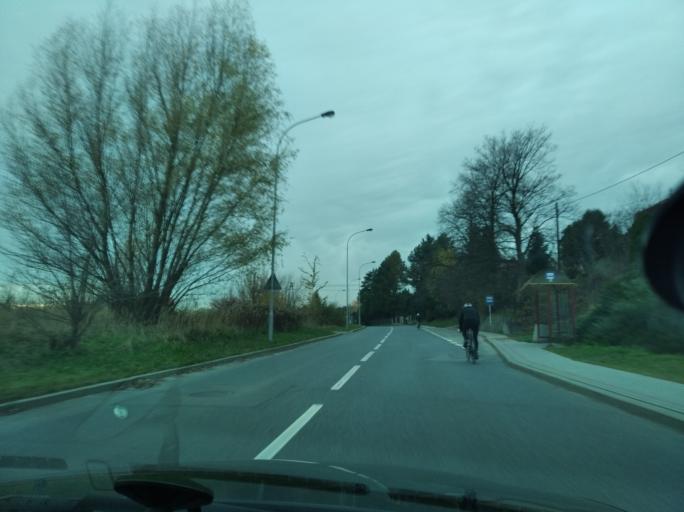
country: PL
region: Subcarpathian Voivodeship
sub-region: Rzeszow
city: Przybyszowka
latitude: 50.0548
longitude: 21.9586
